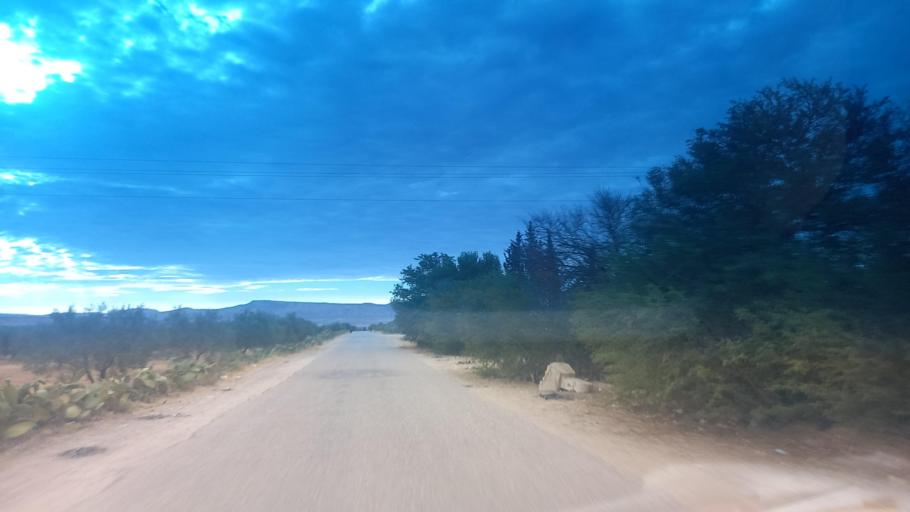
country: TN
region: Al Qasrayn
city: Sbiba
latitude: 35.3803
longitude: 9.0556
